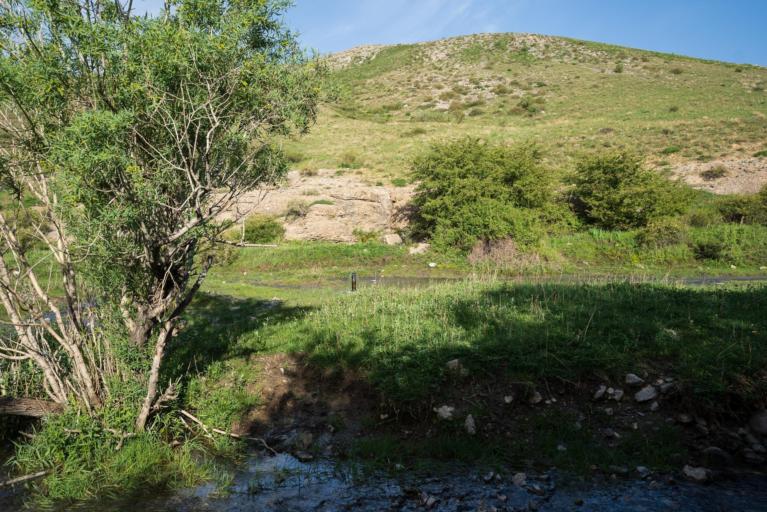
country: KZ
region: Ongtustik Qazaqstan
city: Ashchysay
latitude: 43.6870
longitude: 68.8616
